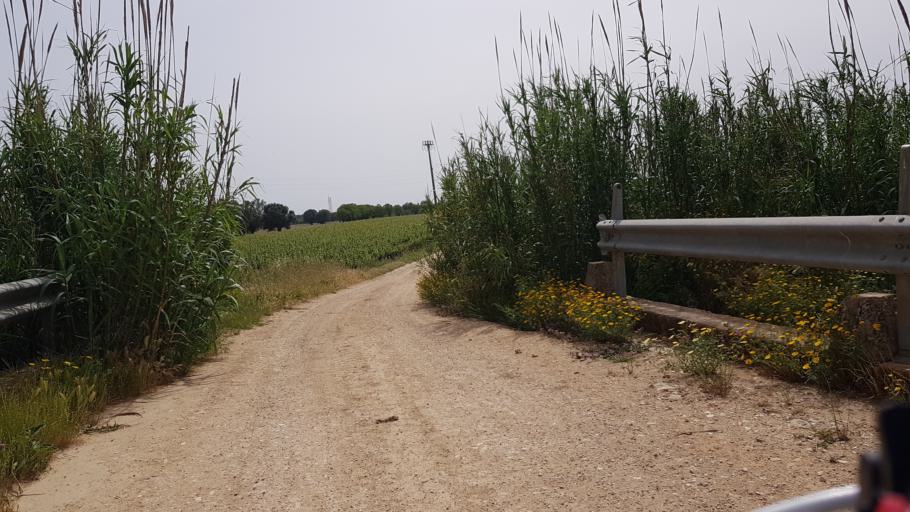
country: IT
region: Apulia
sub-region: Provincia di Brindisi
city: Mesagne
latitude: 40.6324
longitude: 17.8142
